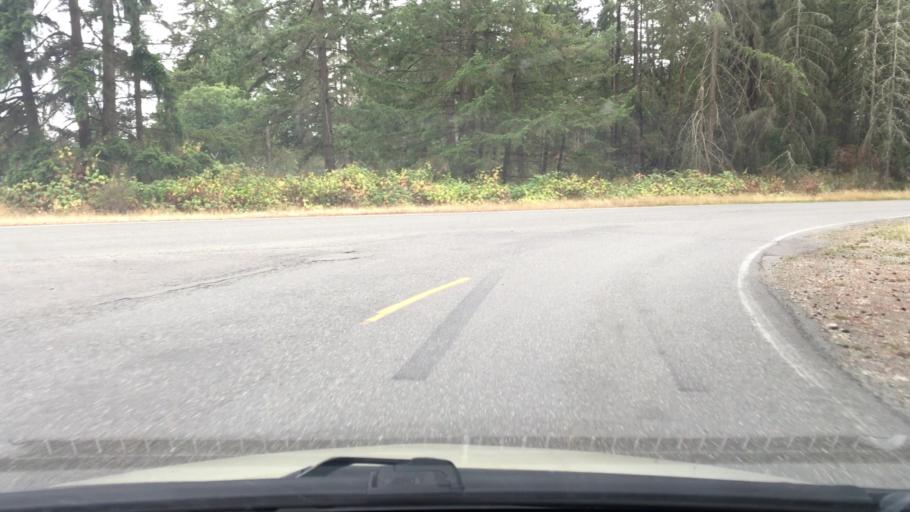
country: US
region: Washington
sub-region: Pierce County
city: Fort Lewis
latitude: 47.1085
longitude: -122.5808
